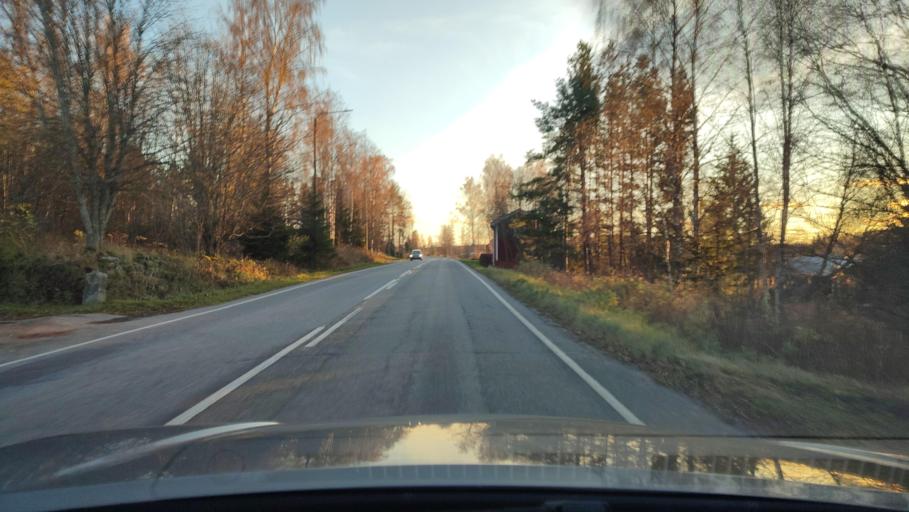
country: FI
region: Ostrobothnia
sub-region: Sydosterbotten
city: Naerpes
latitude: 62.4301
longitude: 21.3472
